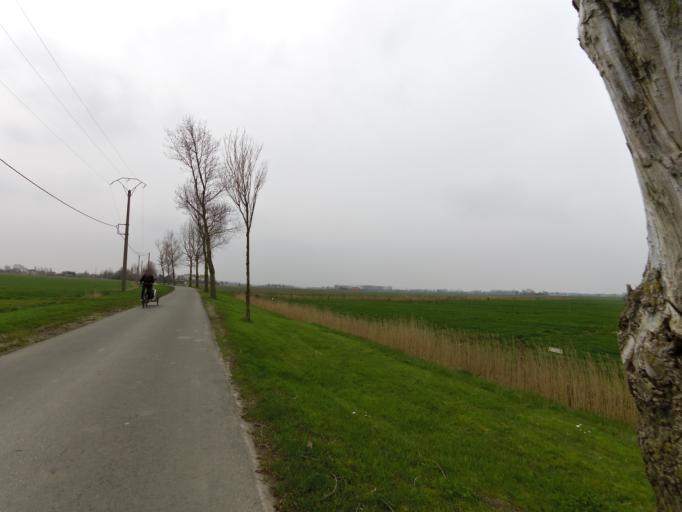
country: BE
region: Flanders
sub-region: Provincie West-Vlaanderen
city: Middelkerke
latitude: 51.1609
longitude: 2.8046
